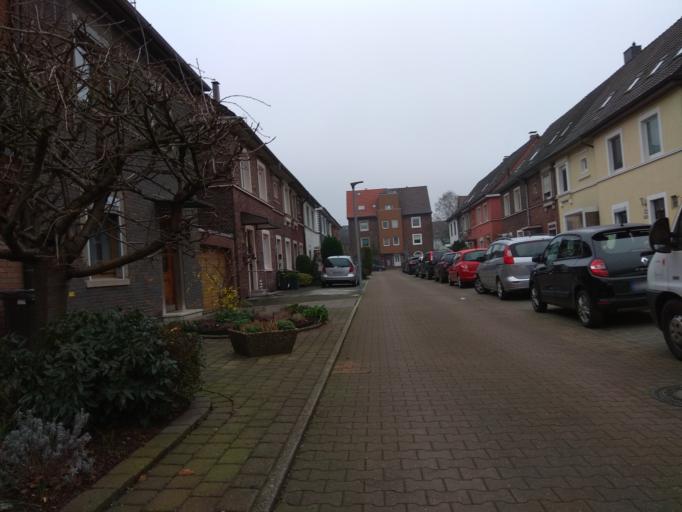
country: DE
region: North Rhine-Westphalia
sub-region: Regierungsbezirk Munster
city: Gelsenkirchen
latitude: 51.4953
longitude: 7.1202
